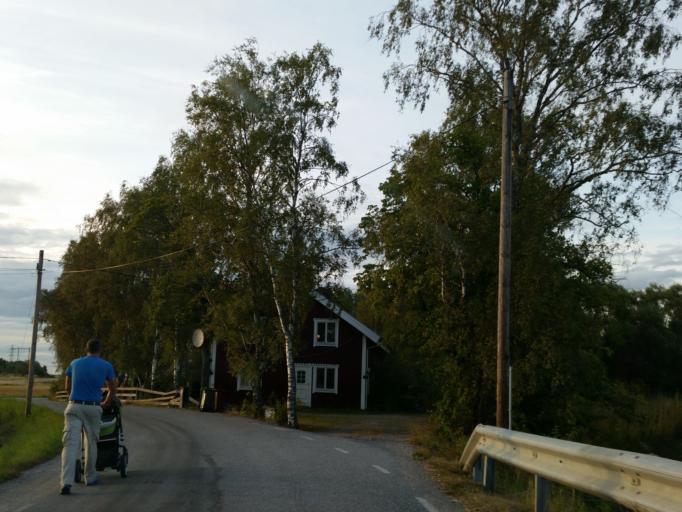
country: SE
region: Stockholm
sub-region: Sigtuna Kommun
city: Marsta
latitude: 59.6334
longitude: 17.8815
